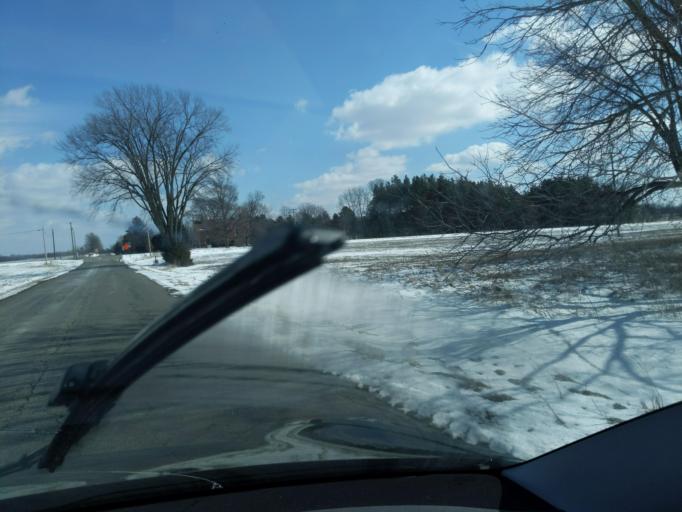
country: US
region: Michigan
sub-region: Ingham County
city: Williamston
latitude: 42.6154
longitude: -84.2815
